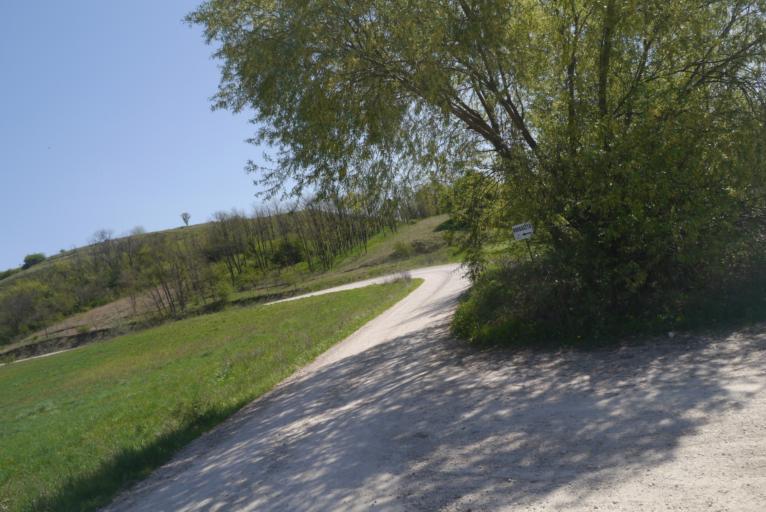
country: HU
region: Komarom-Esztergom
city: Kesztolc
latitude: 47.6983
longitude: 18.7960
